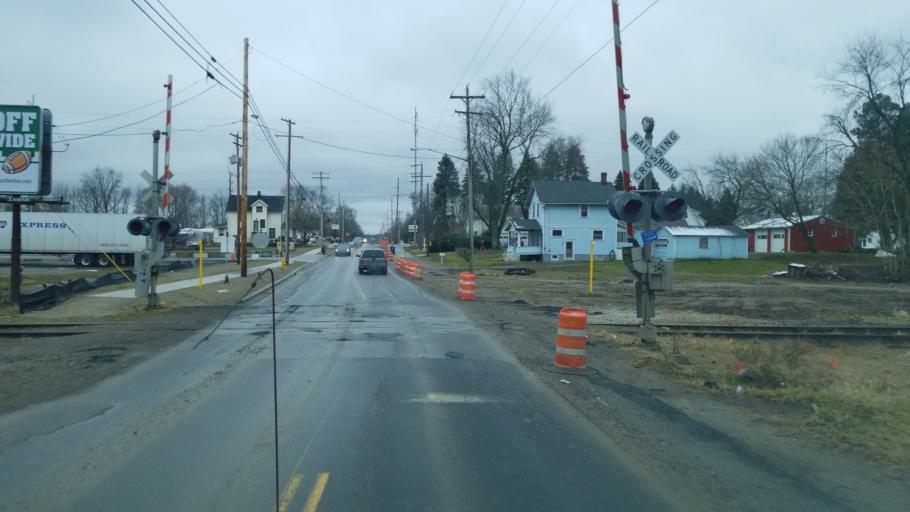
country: US
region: Ohio
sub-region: Summit County
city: Norton
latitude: 41.0193
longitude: -81.6384
